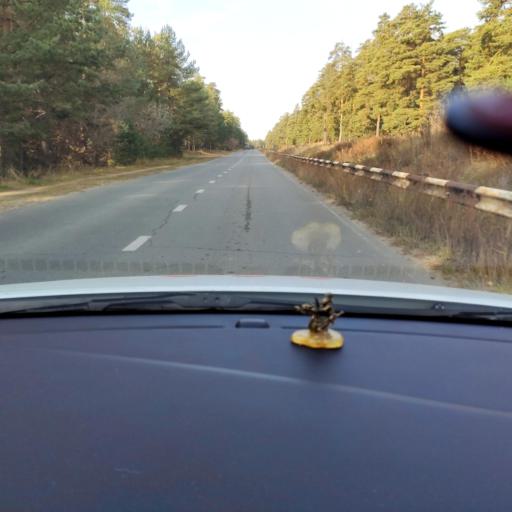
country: RU
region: Tatarstan
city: Staroye Arakchino
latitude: 55.8242
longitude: 48.9121
